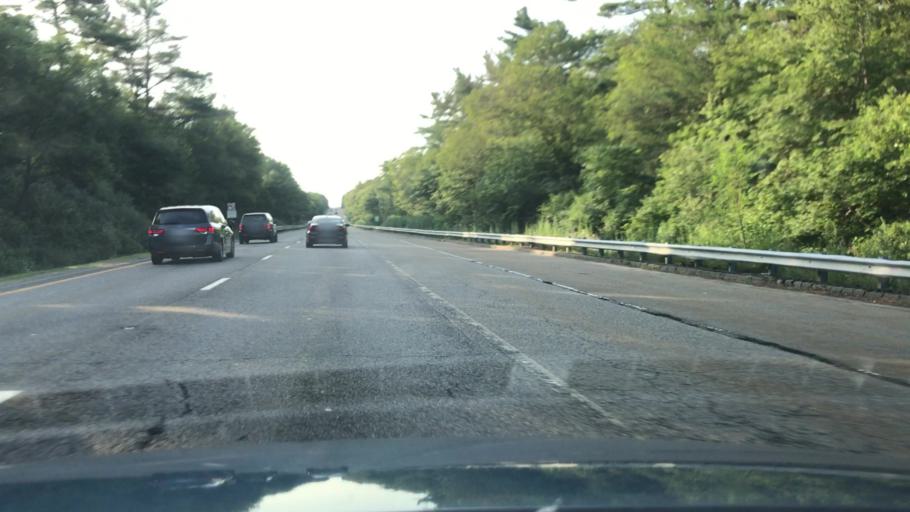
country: US
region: Massachusetts
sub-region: Plymouth County
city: Hanover
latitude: 42.1380
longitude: -70.8210
